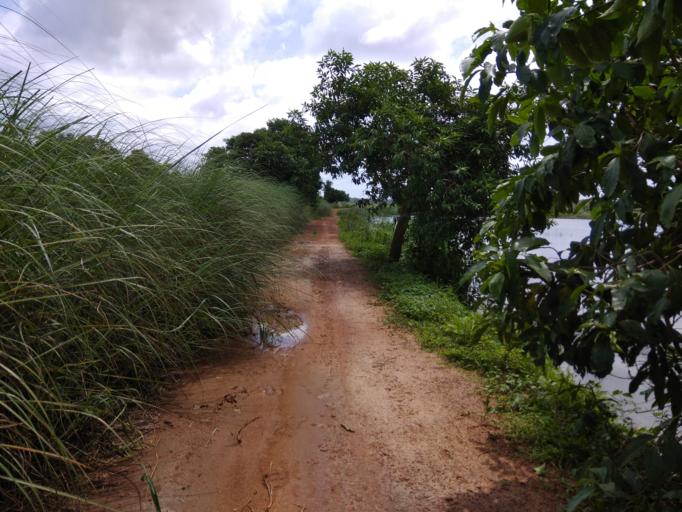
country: IN
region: Kerala
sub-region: Thrissur District
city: Avanoor
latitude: 10.5684
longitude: 76.1362
